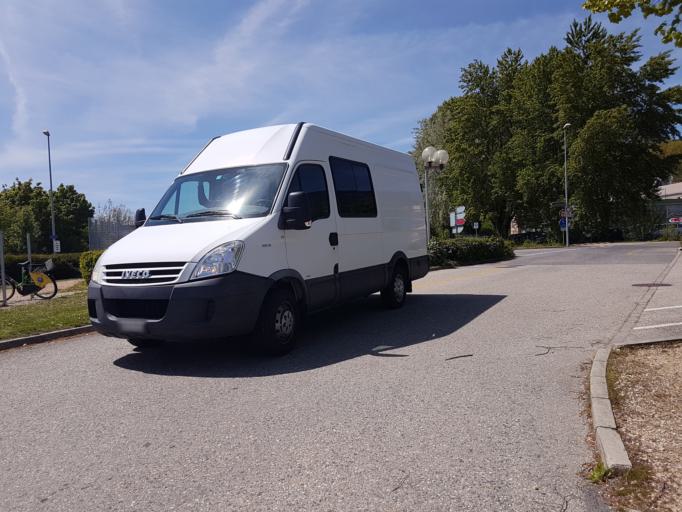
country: CH
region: Neuchatel
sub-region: Neuchatel District
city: Saint-Blaise
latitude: 47.0084
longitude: 6.9727
